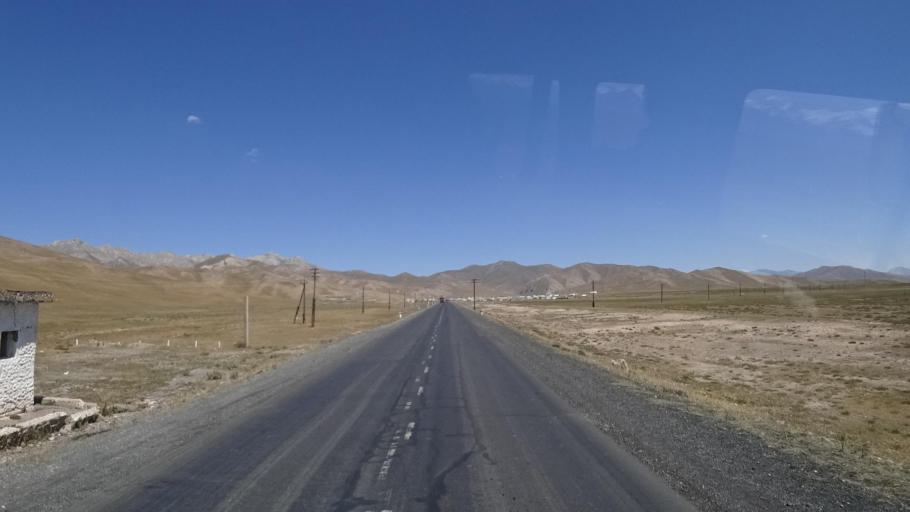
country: KG
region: Osh
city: Gul'cha
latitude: 39.7136
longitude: 73.2379
